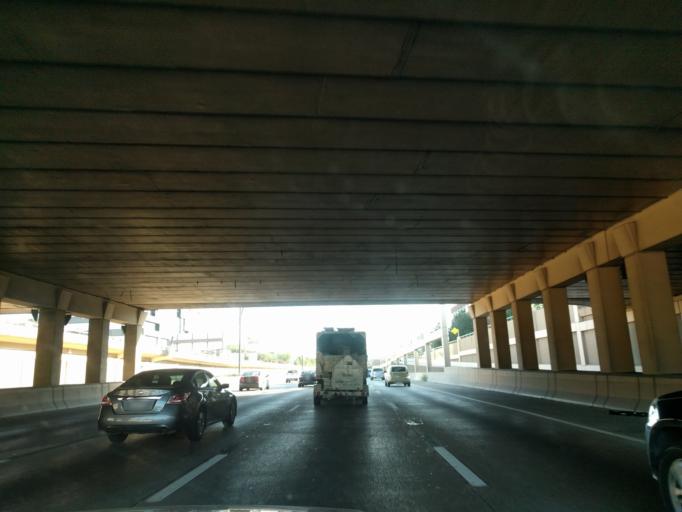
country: US
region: Texas
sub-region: Dallas County
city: Highland Park
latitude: 32.8155
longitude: -96.7894
